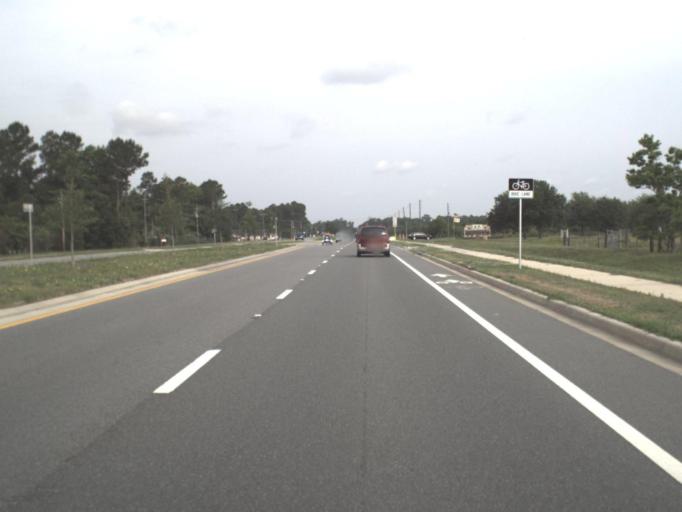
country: US
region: Florida
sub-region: Clay County
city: Green Cove Springs
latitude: 29.9711
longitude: -81.5033
